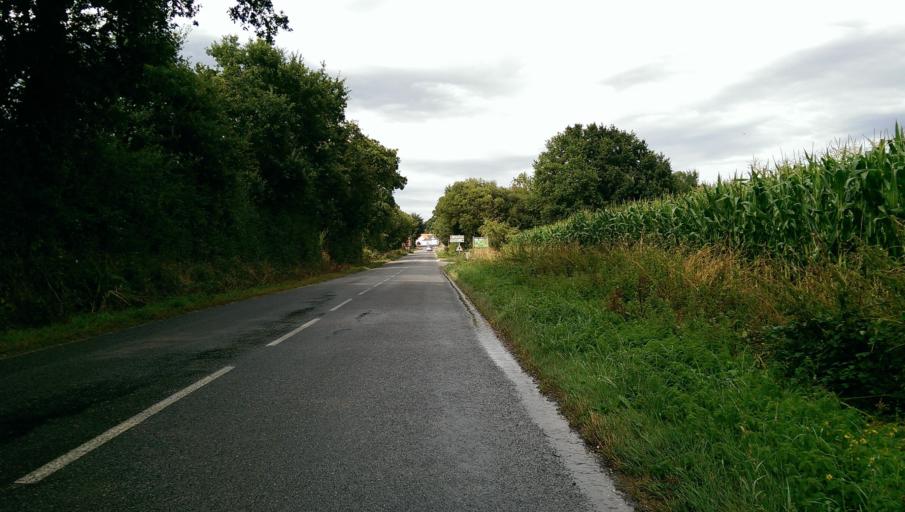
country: FR
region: Pays de la Loire
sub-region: Departement de la Loire-Atlantique
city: La Planche
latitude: 47.0071
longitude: -1.4283
